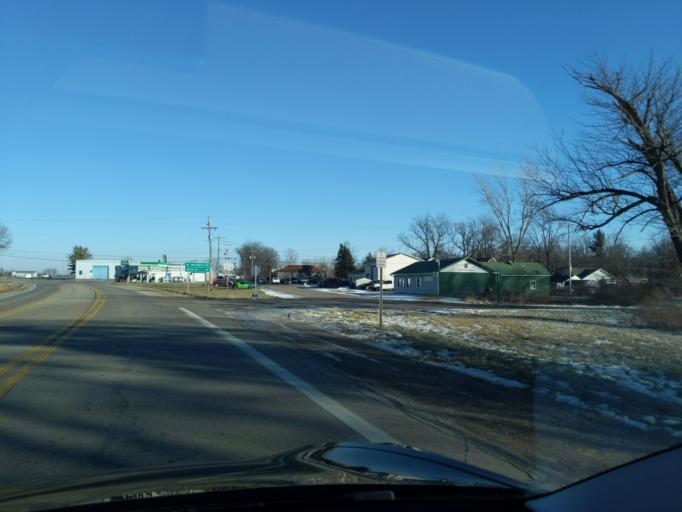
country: US
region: Michigan
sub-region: Ingham County
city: Stockbridge
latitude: 42.3939
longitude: -84.2523
